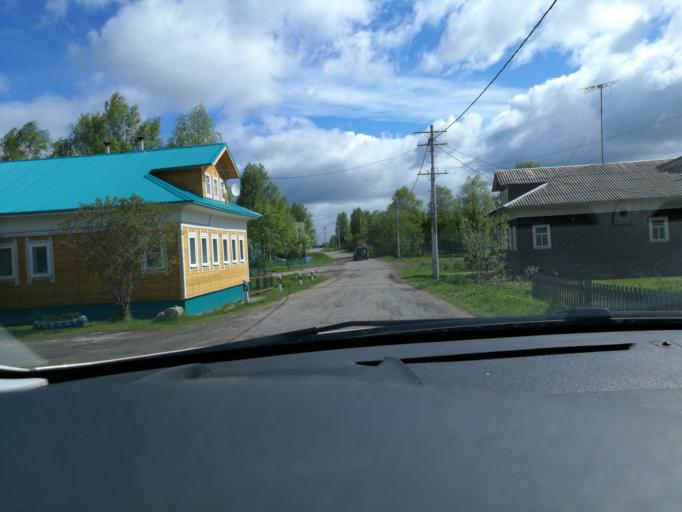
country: RU
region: Arkhangelskaya
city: Kholmogory
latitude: 64.2295
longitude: 41.7364
